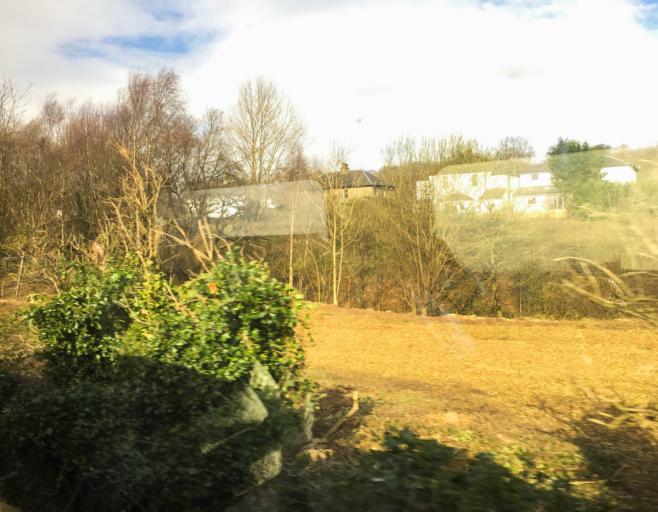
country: GB
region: Scotland
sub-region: East Dunbartonshire
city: Bearsden
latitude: 55.8972
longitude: -4.3214
